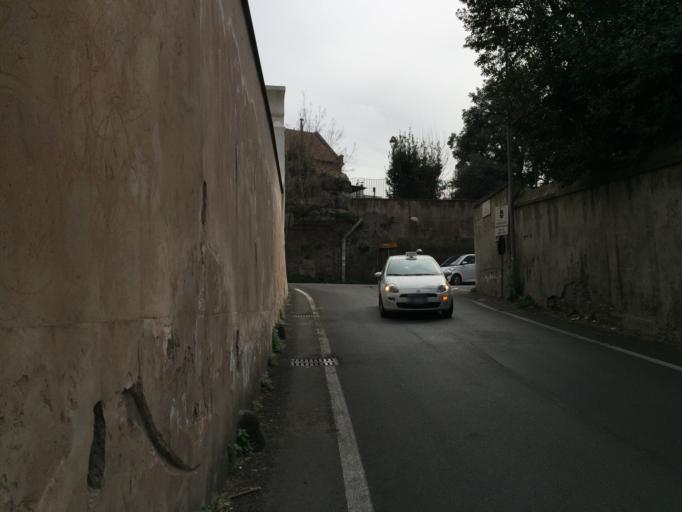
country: VA
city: Vatican City
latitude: 41.8879
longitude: 12.4583
